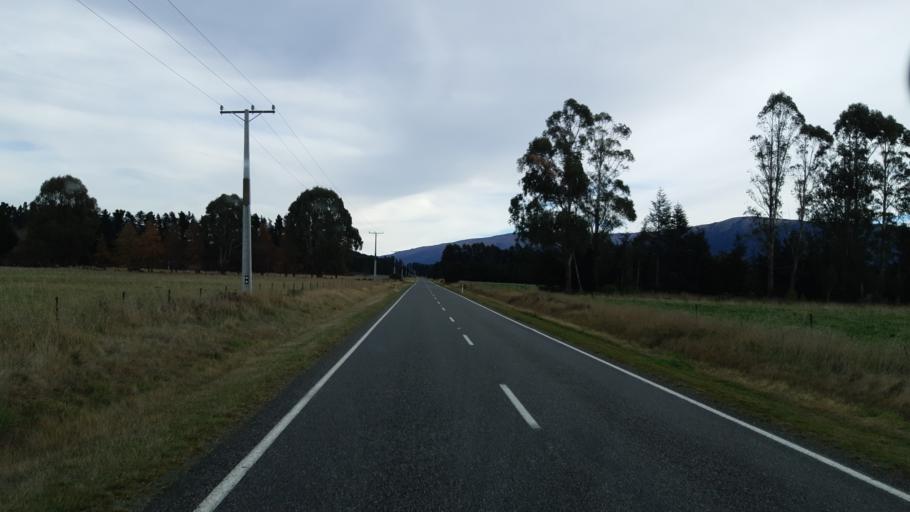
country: NZ
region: Tasman
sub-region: Tasman District
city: Brightwater
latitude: -41.6540
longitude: 173.2539
